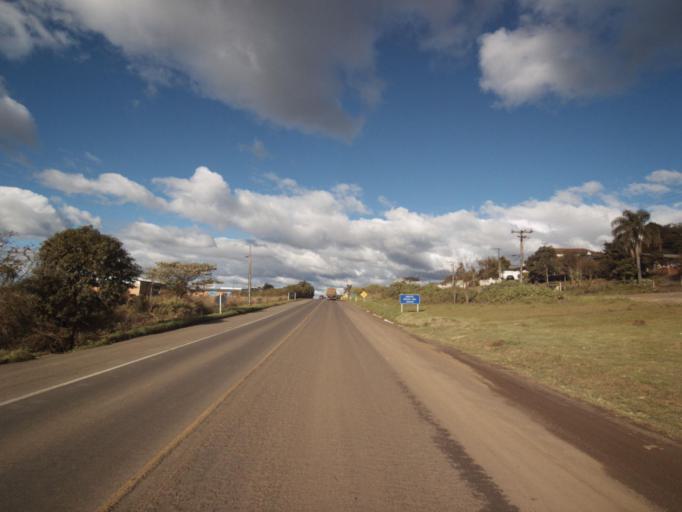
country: BR
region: Santa Catarina
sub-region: Joacaba
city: Joacaba
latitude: -27.1774
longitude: -51.5457
